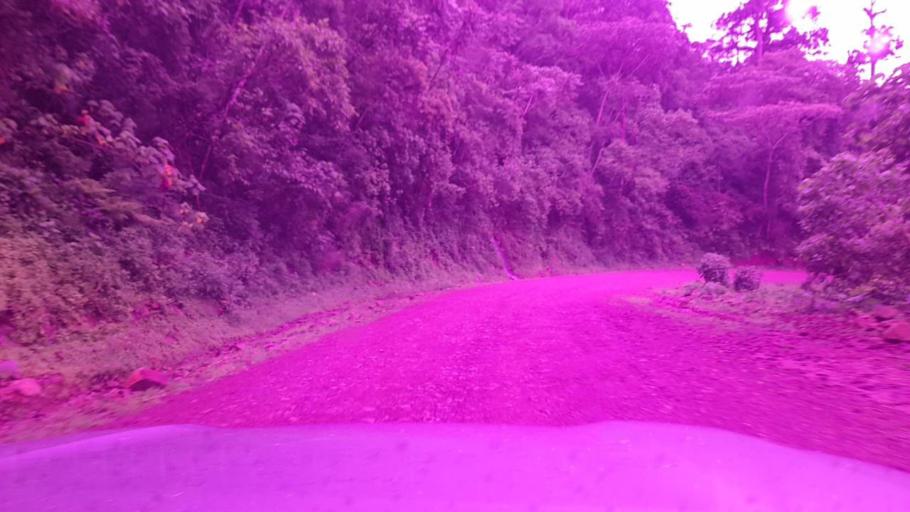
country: ET
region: Southern Nations, Nationalities, and People's Region
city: Bonga
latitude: 7.5105
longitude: 36.0603
